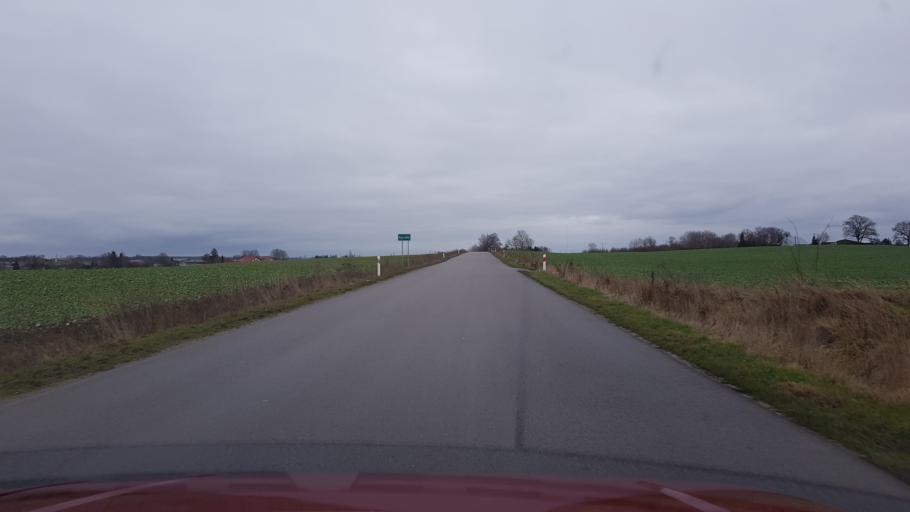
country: PL
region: West Pomeranian Voivodeship
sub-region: Powiat koszalinski
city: Mielno
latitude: 54.1718
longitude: 16.0079
